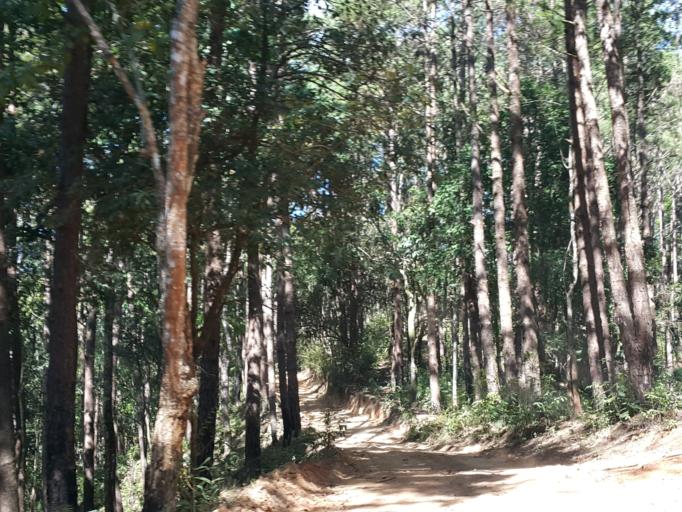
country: TH
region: Chiang Mai
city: Wiang Haeng
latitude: 19.5221
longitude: 98.8115
